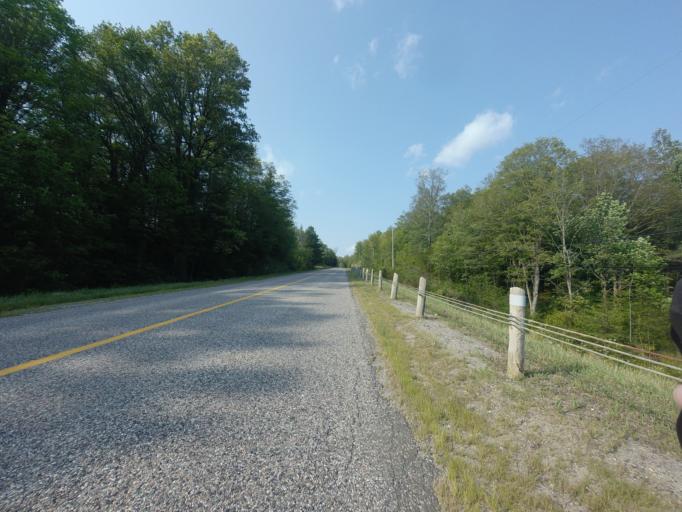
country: CA
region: Ontario
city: Perth
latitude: 44.8195
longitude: -76.7126
